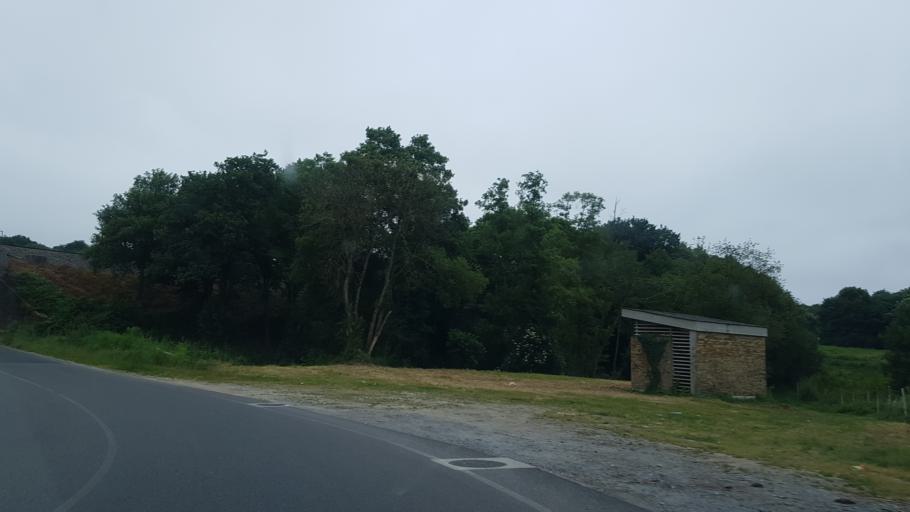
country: ES
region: Galicia
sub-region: Provincia de Lugo
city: Lugo
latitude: 43.0394
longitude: -7.5606
